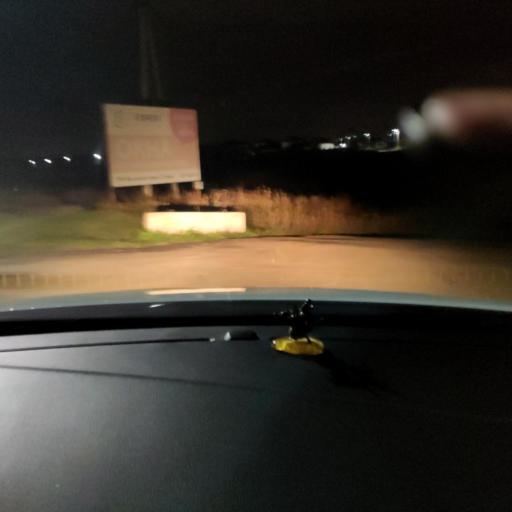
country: RU
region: Tatarstan
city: Vysokaya Gora
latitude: 55.8950
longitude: 49.3043
